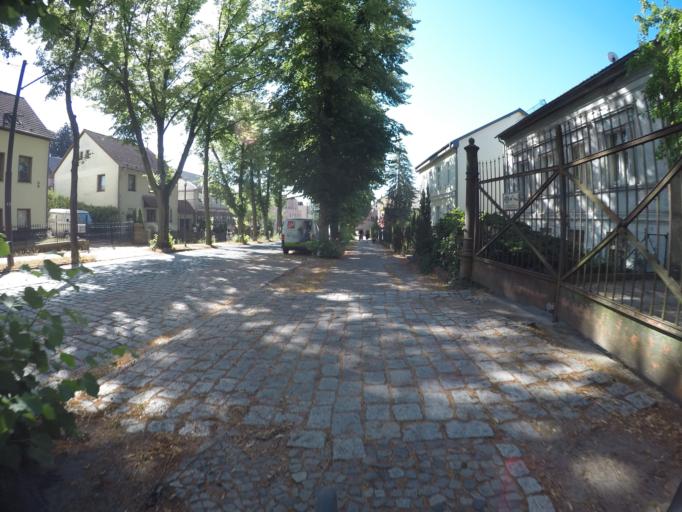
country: DE
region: Brandenburg
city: Woltersdorf
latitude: 52.4444
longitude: 13.7630
